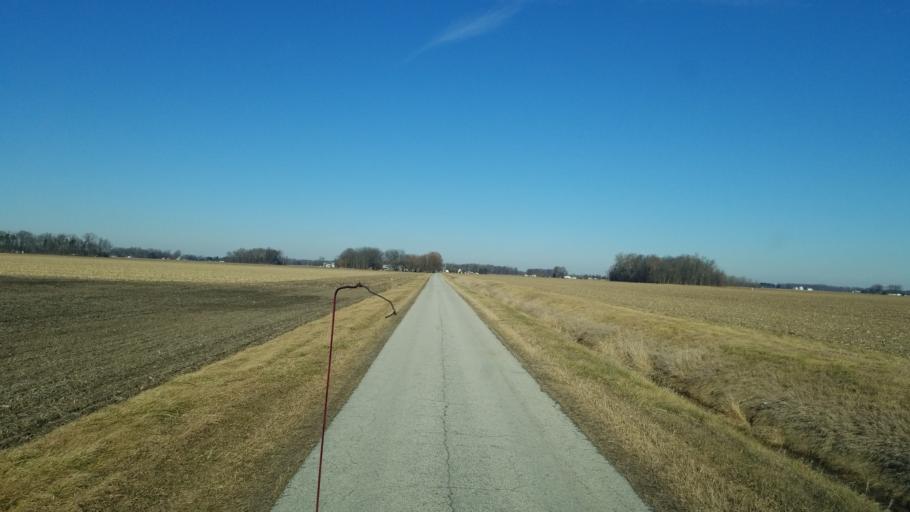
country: US
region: Ohio
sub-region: Henry County
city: Liberty Center
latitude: 41.3598
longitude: -83.9802
